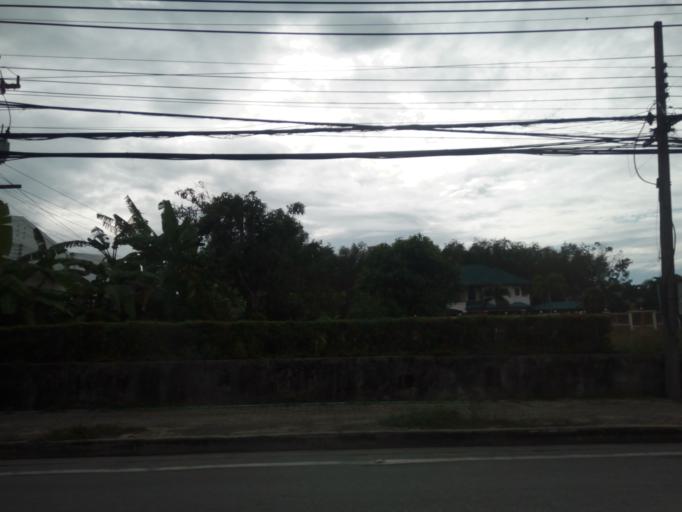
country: TH
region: Phuket
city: Thalang
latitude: 8.0220
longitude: 98.3349
